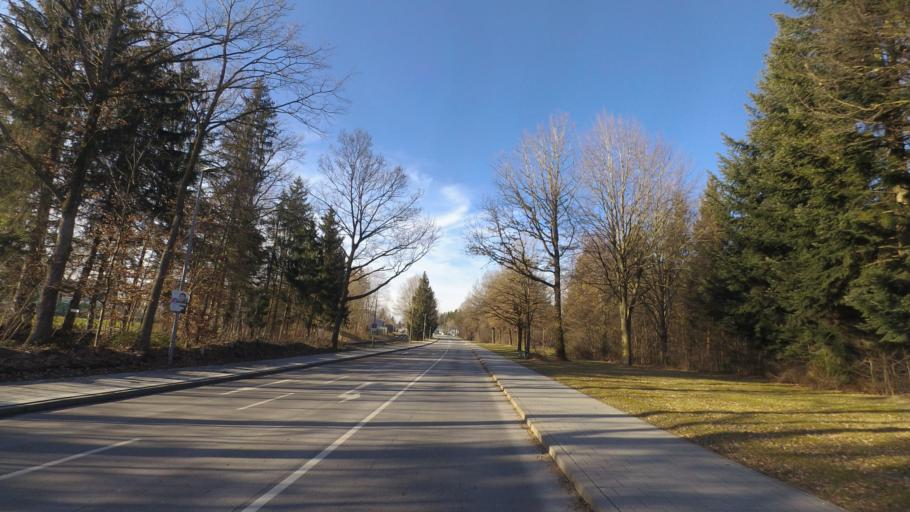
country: DE
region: Bavaria
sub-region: Upper Bavaria
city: Traunreut
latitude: 47.9610
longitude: 12.6050
